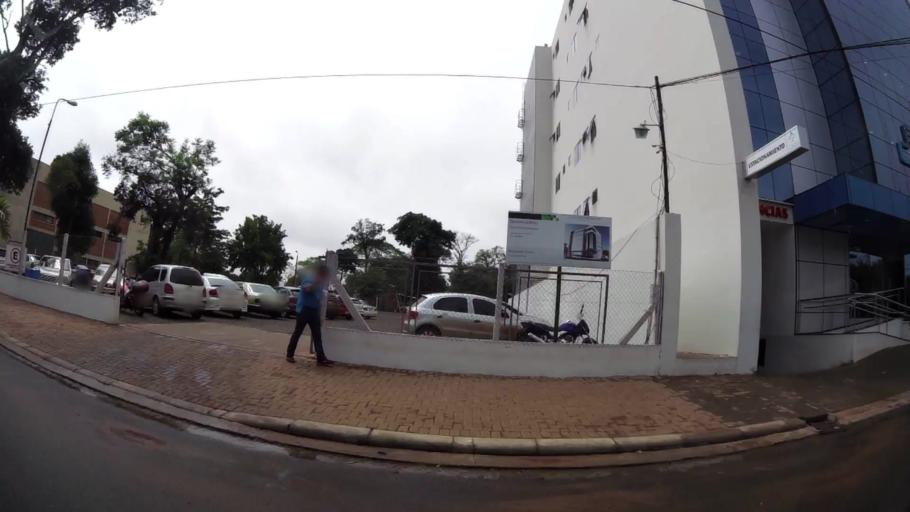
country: PY
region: Alto Parana
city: Ciudad del Este
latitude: -25.5139
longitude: -54.6450
